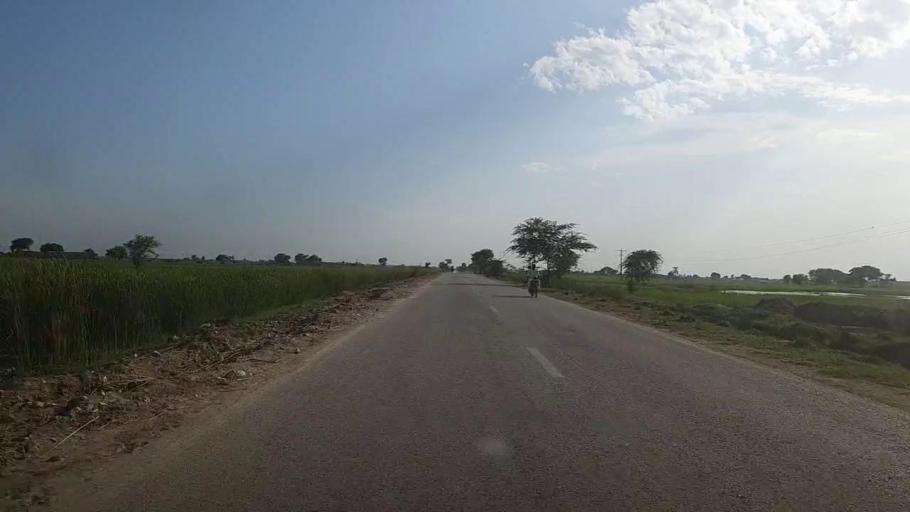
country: PK
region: Sindh
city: Thul
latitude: 28.2084
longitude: 68.7476
